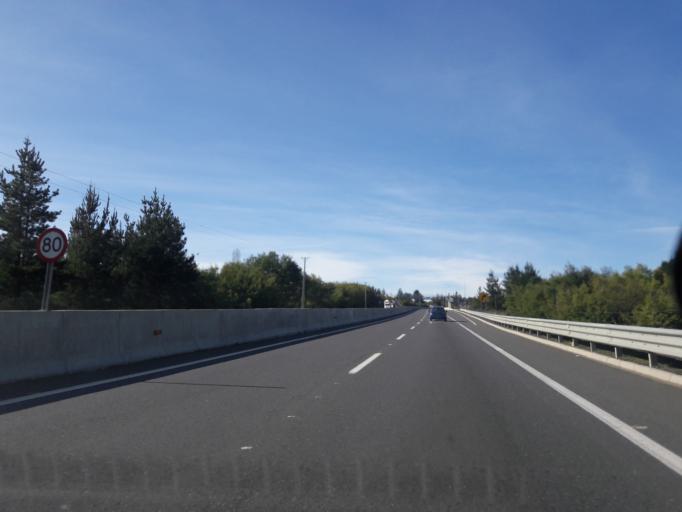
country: CL
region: Biobio
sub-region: Provincia de Biobio
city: Yumbel
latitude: -36.9742
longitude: -72.6597
